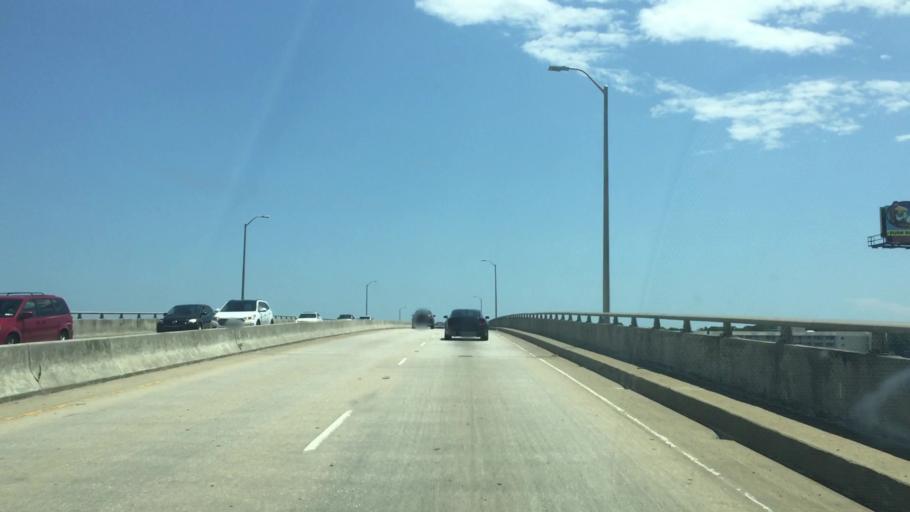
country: US
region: South Carolina
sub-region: Horry County
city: Little River
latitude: 33.8544
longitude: -78.6547
